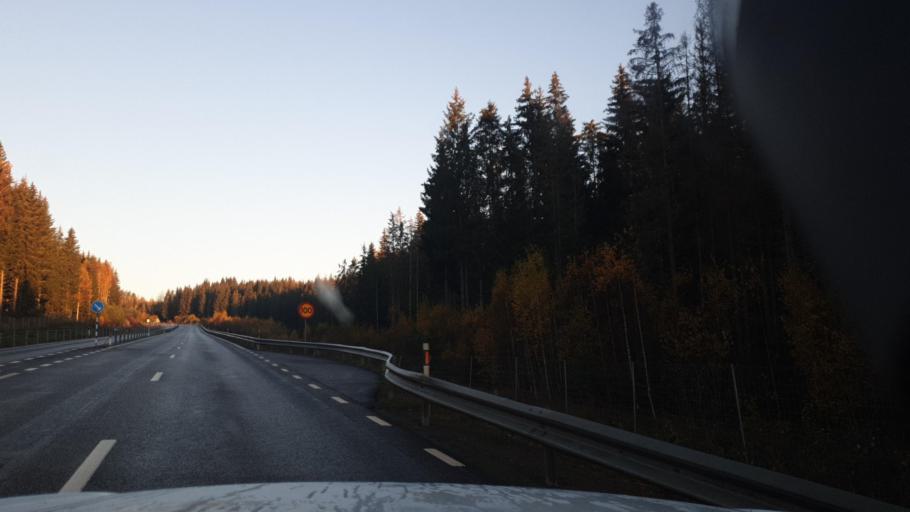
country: SE
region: Vaermland
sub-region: Eda Kommun
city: Amotfors
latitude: 59.7564
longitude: 12.4769
